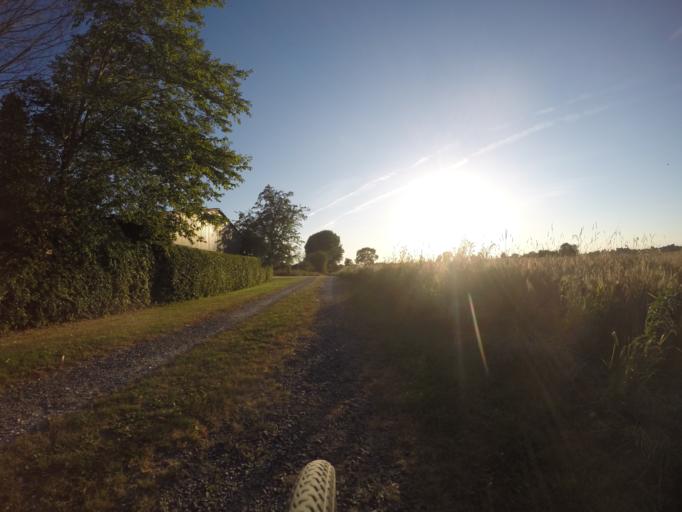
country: DK
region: Capital Region
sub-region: Egedal Kommune
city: Smorumnedre
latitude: 55.7005
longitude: 12.3172
